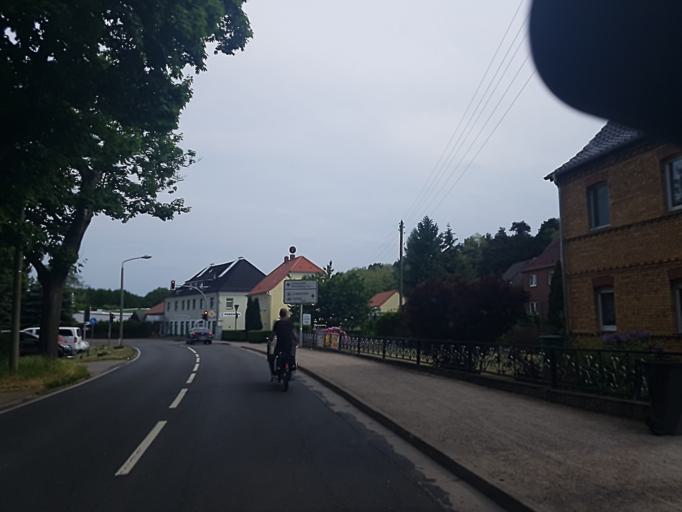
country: DE
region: Saxony-Anhalt
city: Nudersdorf
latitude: 51.9020
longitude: 12.6115
